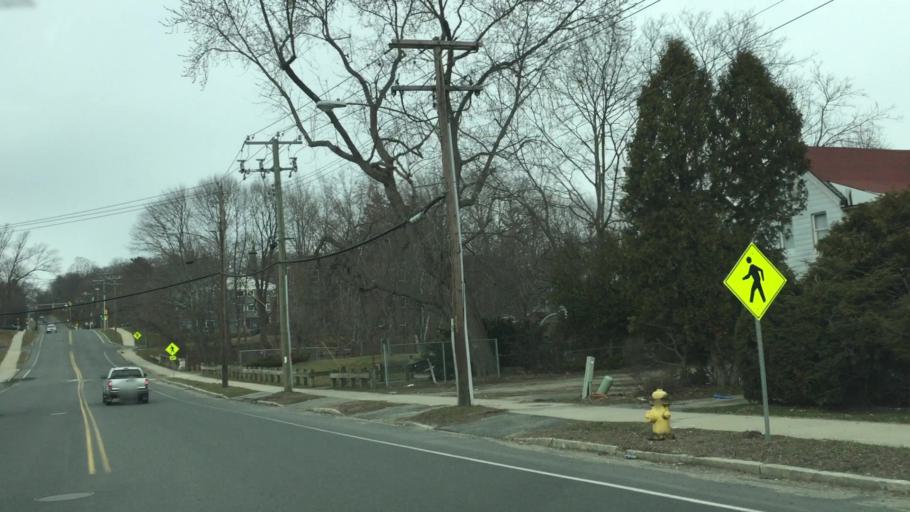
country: US
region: Massachusetts
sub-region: Berkshire County
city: Pittsfield
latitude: 42.4498
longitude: -73.2621
